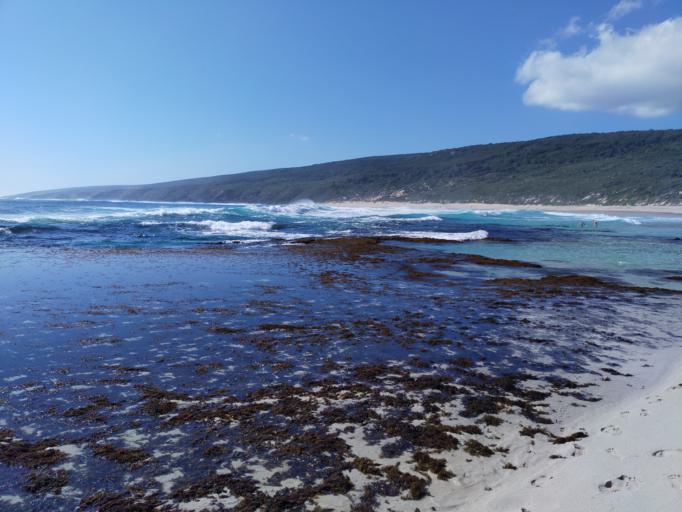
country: AU
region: Western Australia
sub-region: Busselton
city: Yallingup
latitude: -33.6376
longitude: 115.0257
